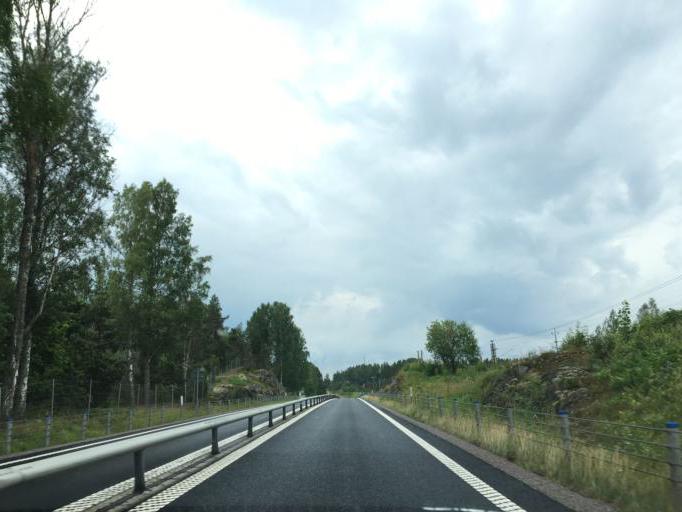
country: SE
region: Soedermanland
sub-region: Katrineholms Kommun
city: Katrineholm
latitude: 58.8732
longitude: 16.1975
